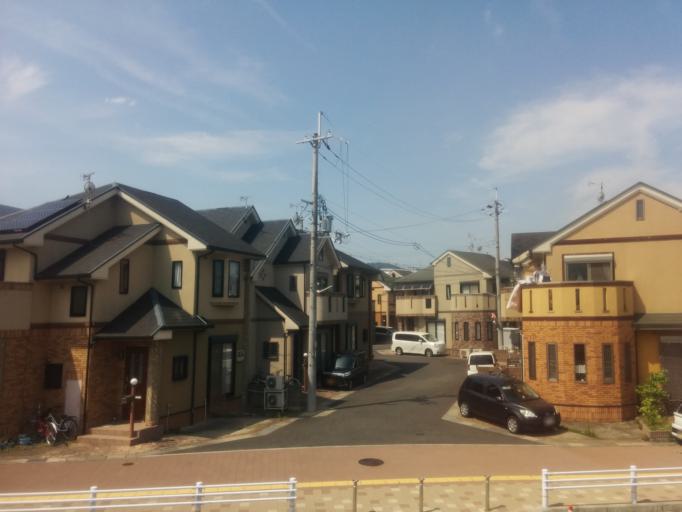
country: JP
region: Kyoto
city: Kameoka
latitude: 35.0120
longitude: 135.5891
